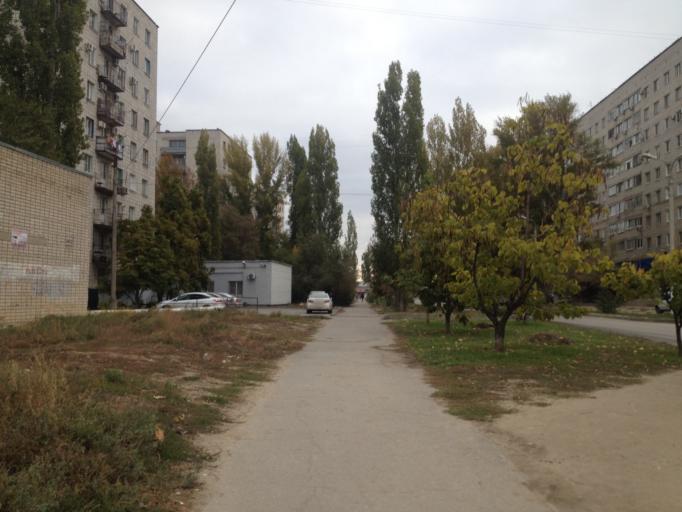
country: RU
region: Volgograd
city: Volgograd
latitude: 48.7362
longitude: 44.4888
